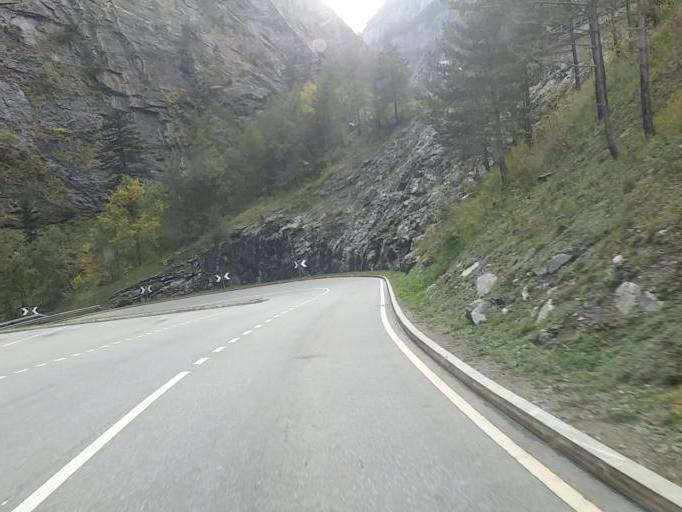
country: IT
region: Piedmont
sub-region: Provincia Verbano-Cusio-Ossola
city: Trasquera
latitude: 46.1983
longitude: 8.1269
